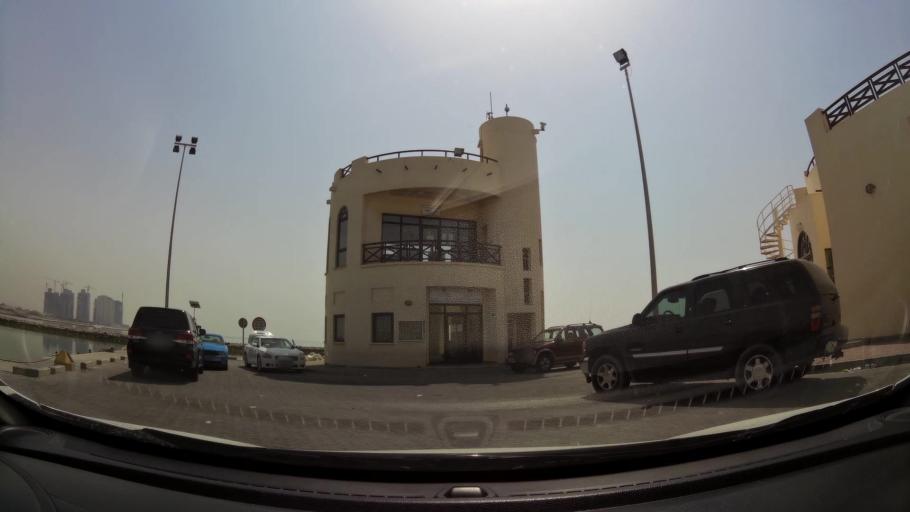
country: BH
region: Manama
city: Jidd Hafs
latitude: 26.2141
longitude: 50.4408
